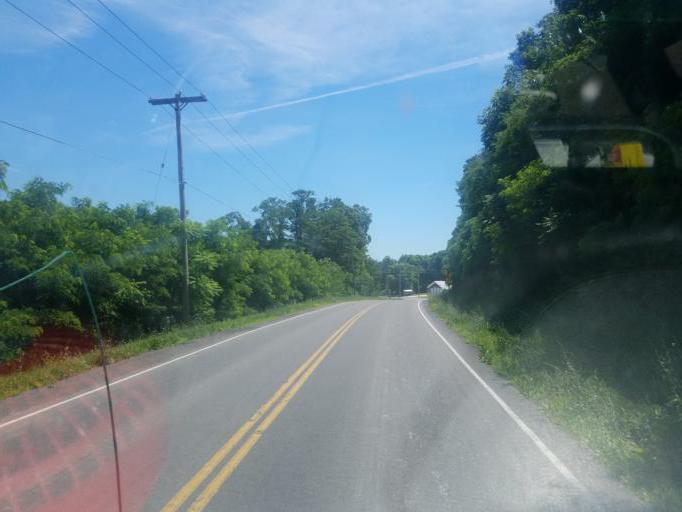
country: US
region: New York
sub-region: Yates County
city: Dundee
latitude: 42.5952
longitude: -76.9610
